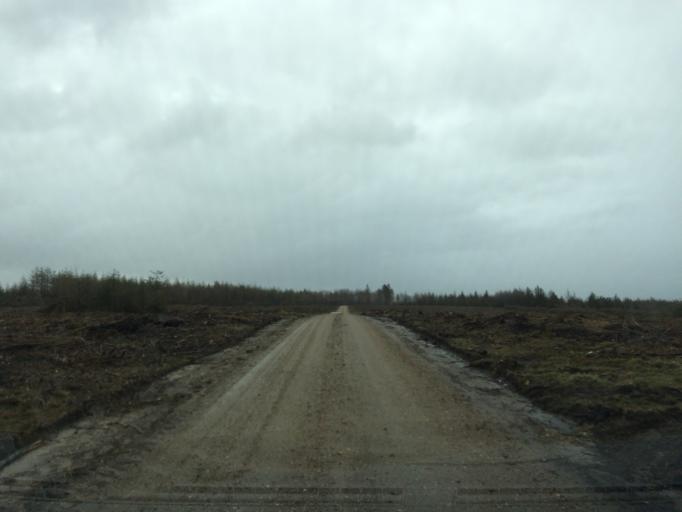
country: DK
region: Central Jutland
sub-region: Holstebro Kommune
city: Holstebro
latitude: 56.2193
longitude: 8.5155
